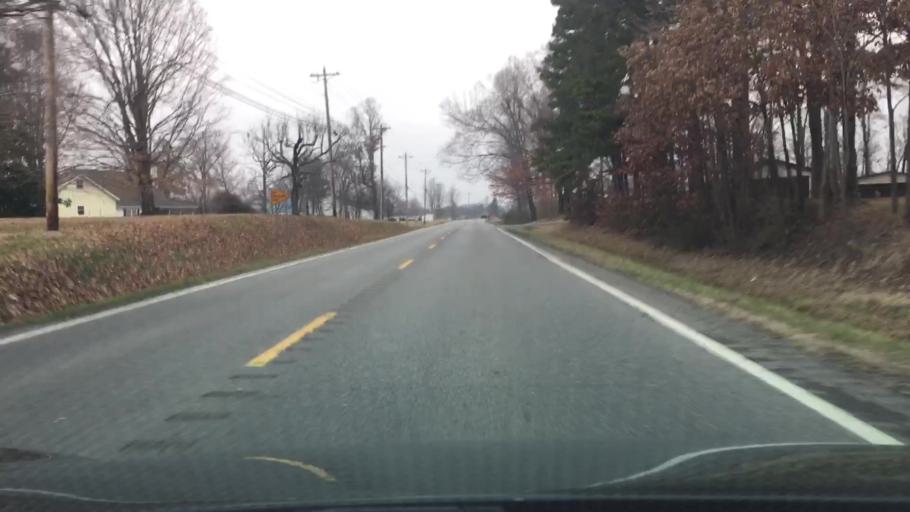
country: US
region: Kentucky
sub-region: Marshall County
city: Benton
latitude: 36.9404
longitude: -88.3604
